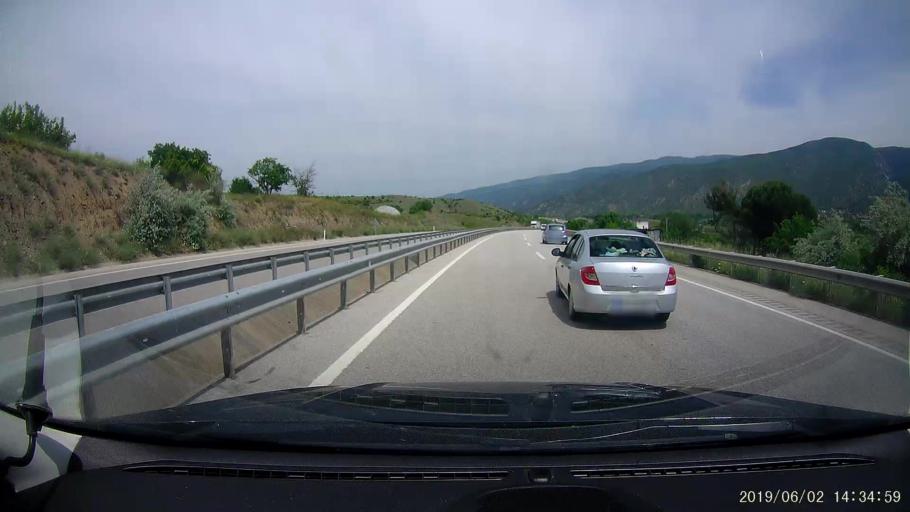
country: TR
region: Kastamonu
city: Tosya
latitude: 41.0410
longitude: 34.2061
